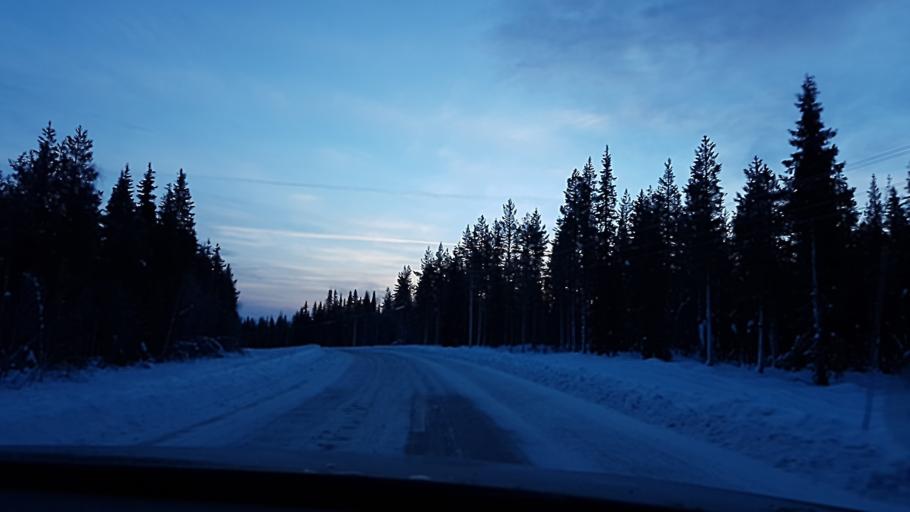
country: SE
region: Norrbotten
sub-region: Jokkmokks Kommun
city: Jokkmokk
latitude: 66.1296
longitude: 20.0038
